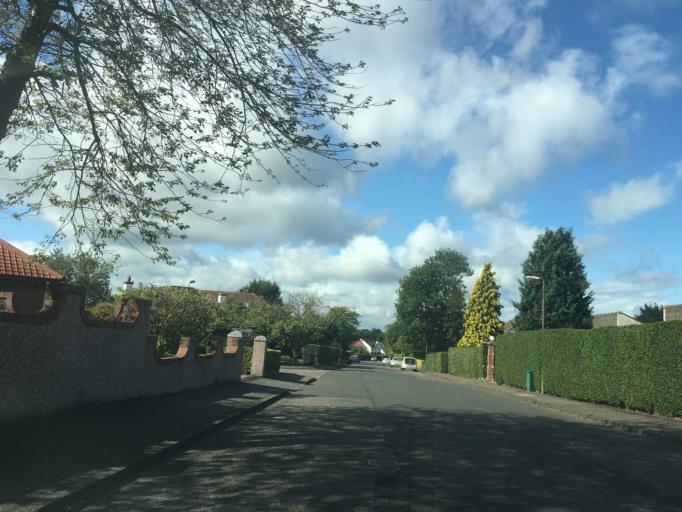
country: GB
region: Scotland
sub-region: Edinburgh
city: Currie
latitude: 55.9598
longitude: -3.3089
